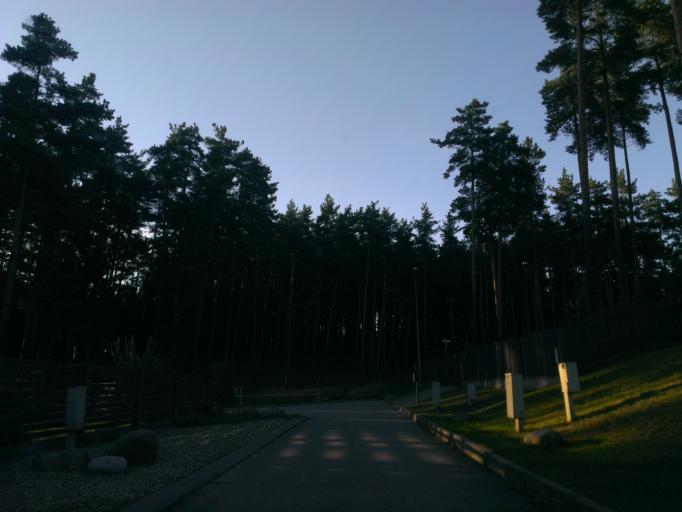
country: LV
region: Riga
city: Bergi
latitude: 56.9791
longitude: 24.3093
